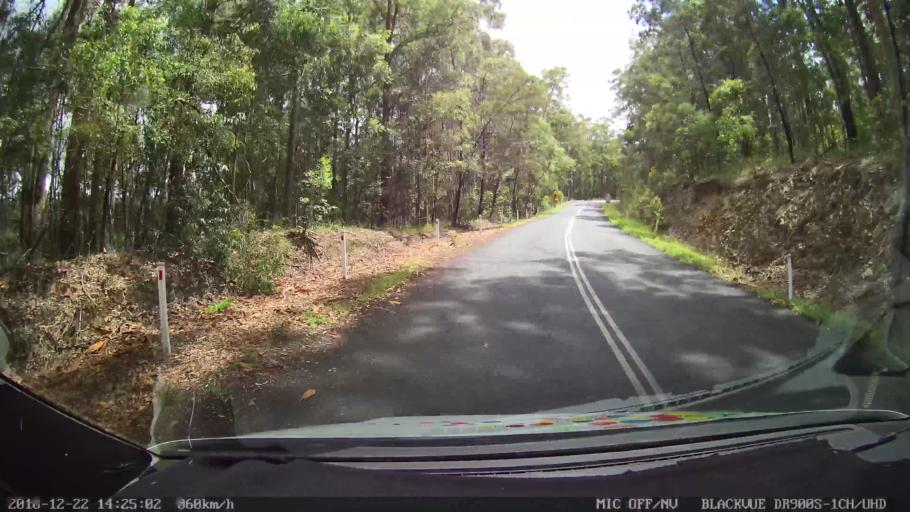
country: AU
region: New South Wales
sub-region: Bellingen
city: Dorrigo
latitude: -30.0490
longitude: 152.6420
